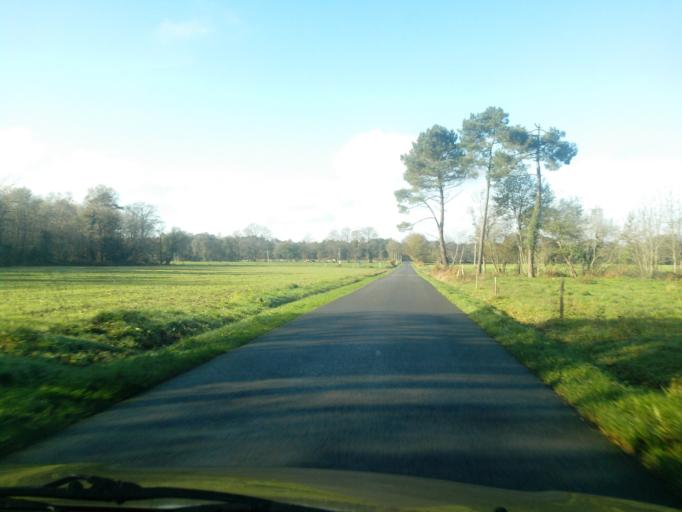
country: FR
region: Brittany
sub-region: Departement du Morbihan
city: Pleucadeuc
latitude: 47.7270
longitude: -2.3930
